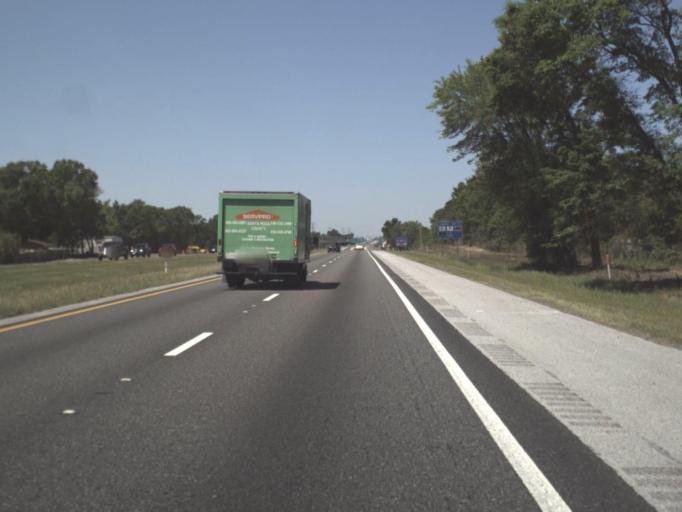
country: US
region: Florida
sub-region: Escambia County
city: Ferry Pass
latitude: 30.5029
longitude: -87.1990
